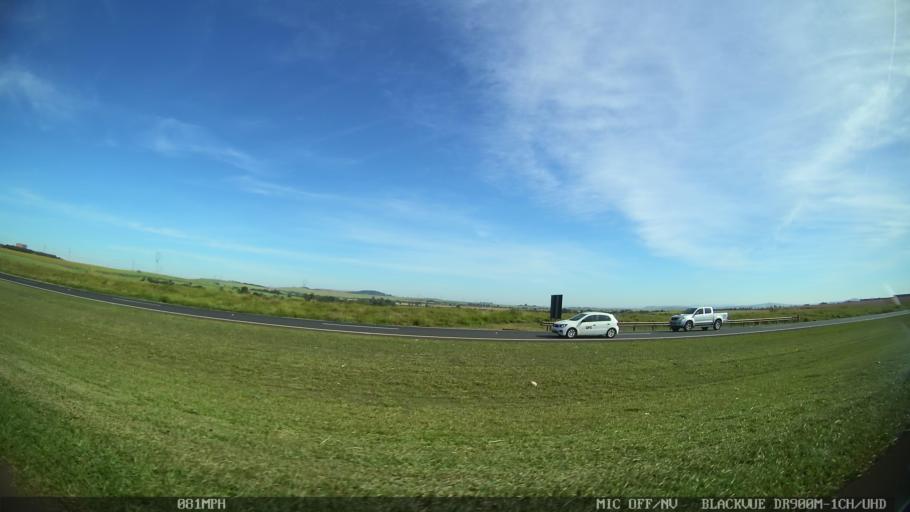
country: BR
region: Sao Paulo
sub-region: Araras
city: Araras
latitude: -22.4277
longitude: -47.3936
